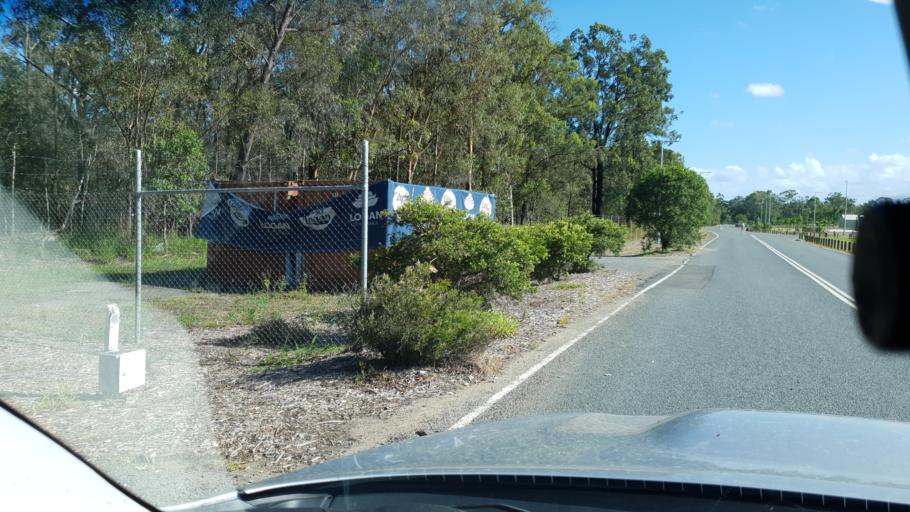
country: AU
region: Queensland
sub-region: Logan
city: Woodridge
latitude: -27.6707
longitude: 153.0707
